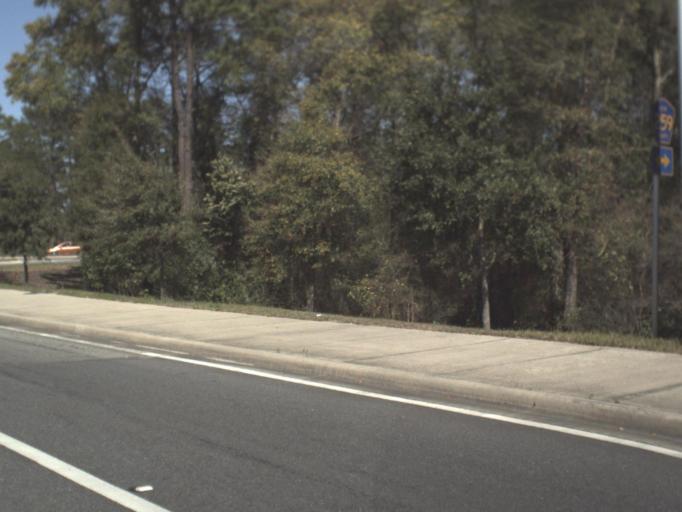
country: US
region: Florida
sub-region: Leon County
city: Woodville
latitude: 30.3803
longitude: -84.2368
